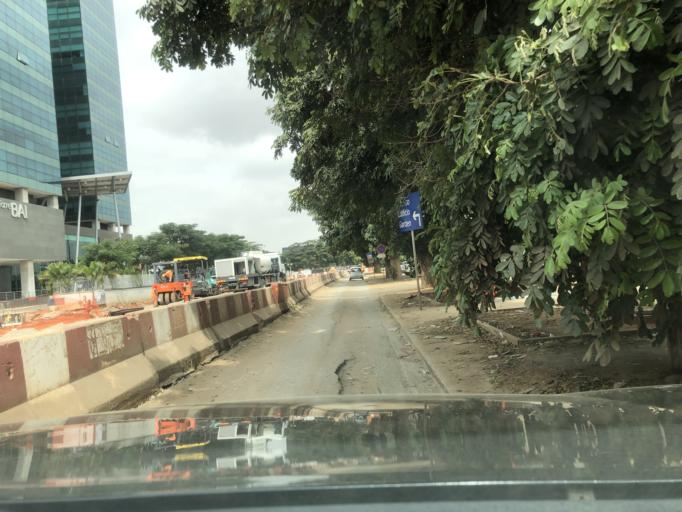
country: AO
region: Luanda
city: Luanda
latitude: -8.8370
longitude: 13.2343
